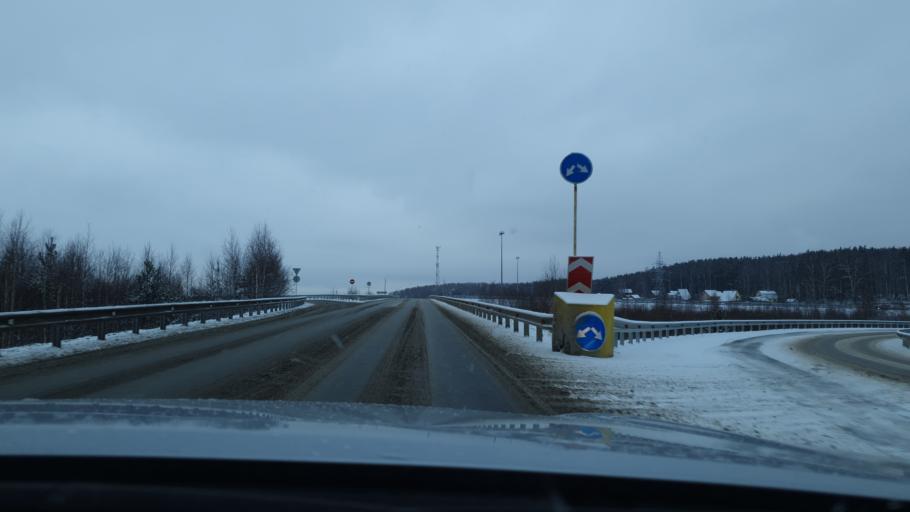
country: RU
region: Sverdlovsk
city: Istok
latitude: 56.7713
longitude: 60.7374
